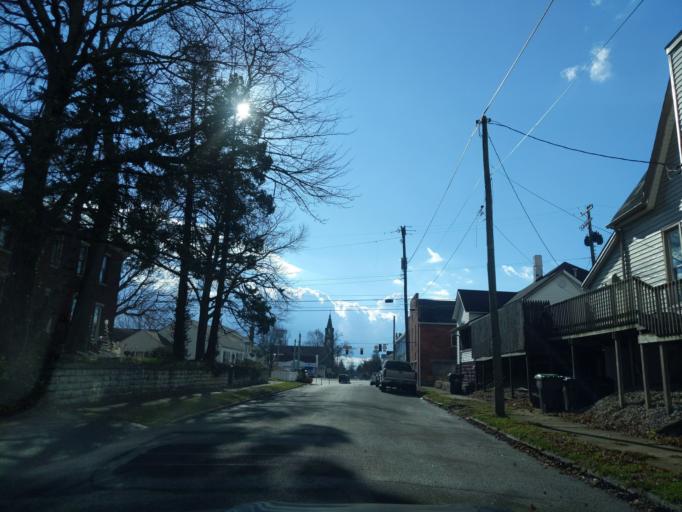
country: US
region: Indiana
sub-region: Decatur County
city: Greensburg
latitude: 39.3376
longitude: -85.4815
